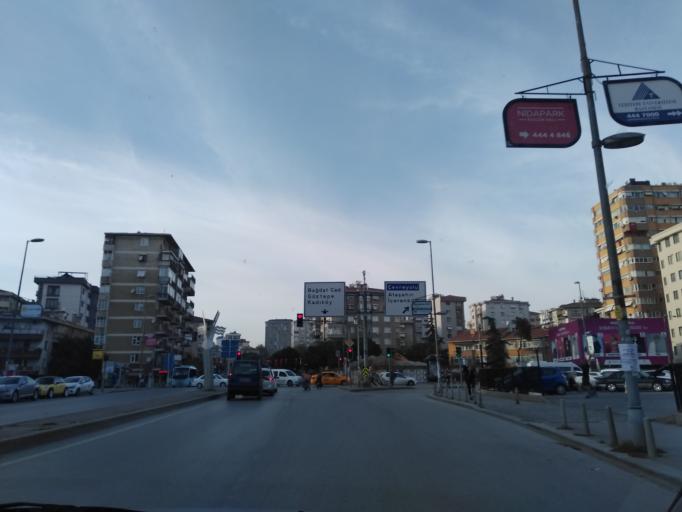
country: TR
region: Istanbul
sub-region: Atasehir
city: Atasehir
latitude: 40.9557
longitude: 29.1003
